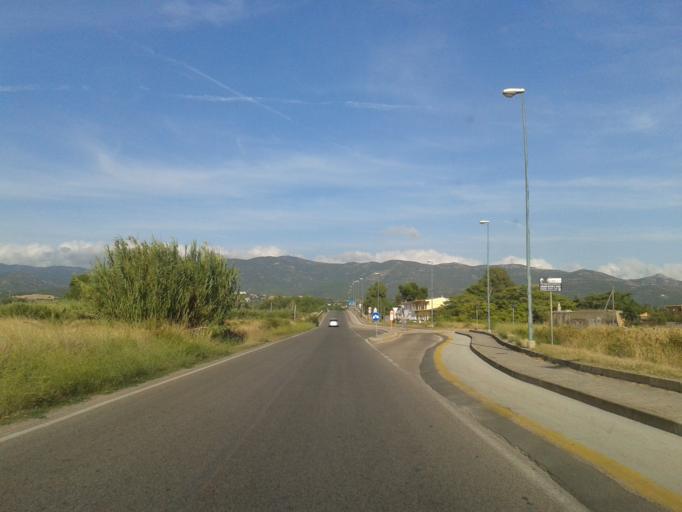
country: IT
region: Sardinia
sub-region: Provincia di Cagliari
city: Quartu Sant'Elena
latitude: 39.2176
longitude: 9.2879
